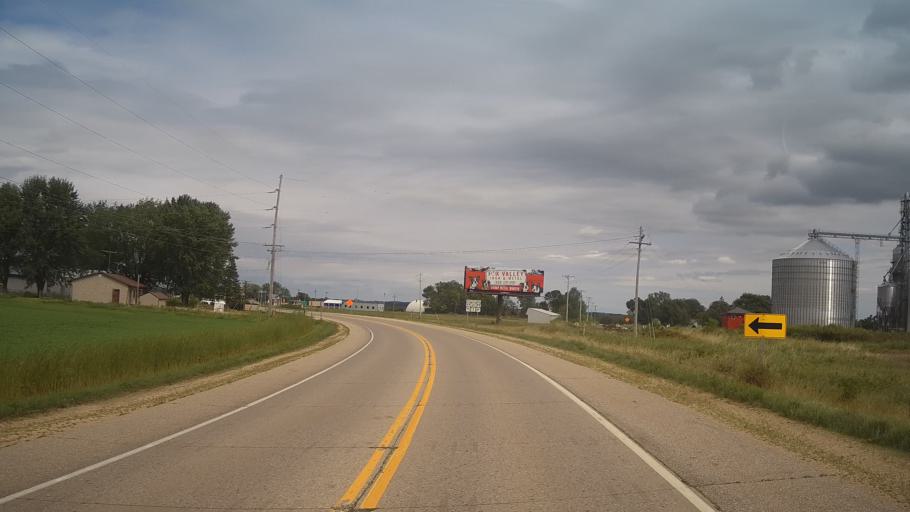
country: US
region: Wisconsin
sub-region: Green Lake County
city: Berlin
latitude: 44.0412
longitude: -88.9881
